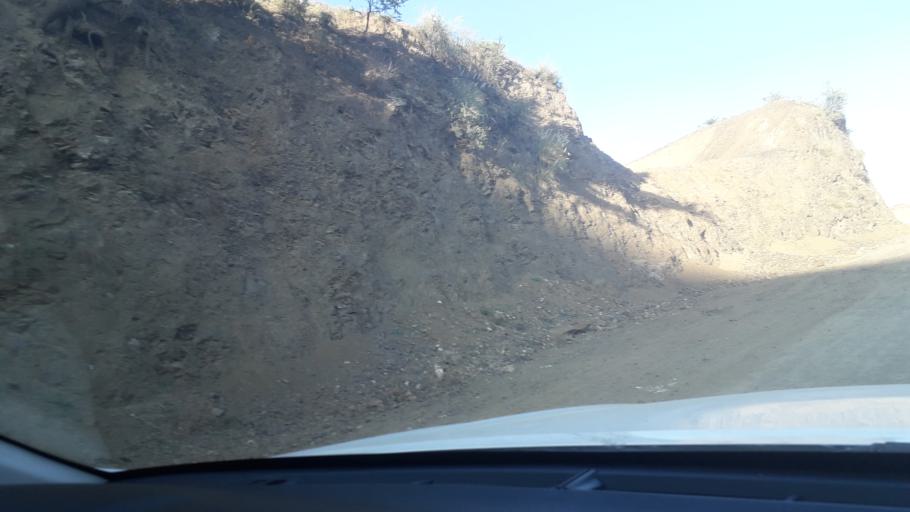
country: ET
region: Amhara
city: Dese
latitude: 11.5210
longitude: 39.2512
